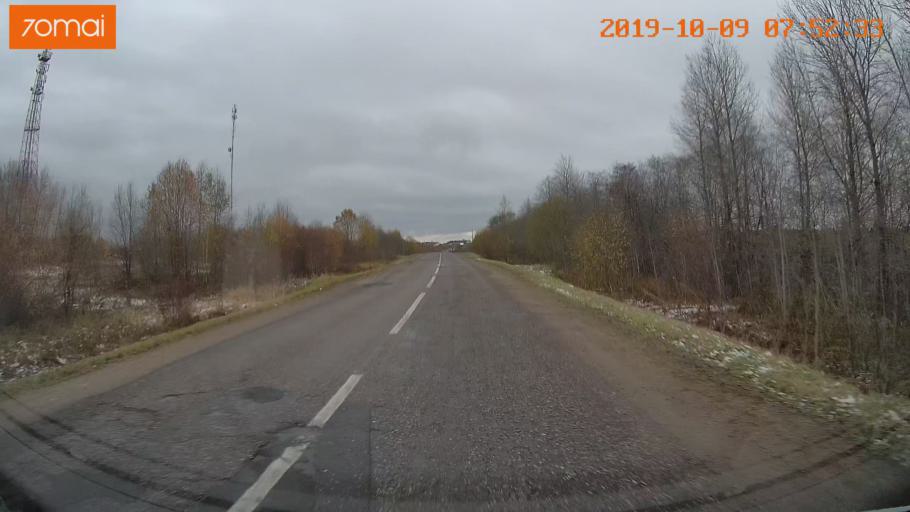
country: RU
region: Jaroslavl
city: Kukoboy
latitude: 58.6921
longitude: 39.8882
